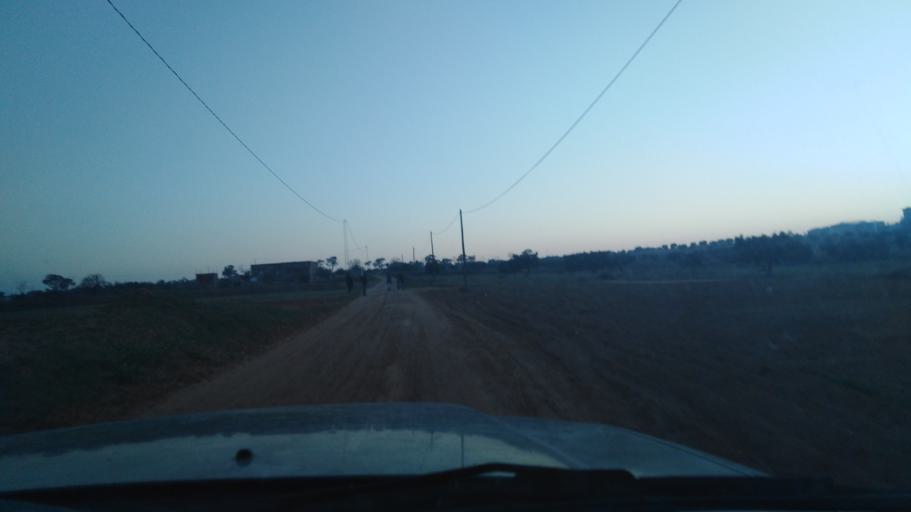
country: TN
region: Safaqis
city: Sfax
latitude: 34.7320
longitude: 10.4872
